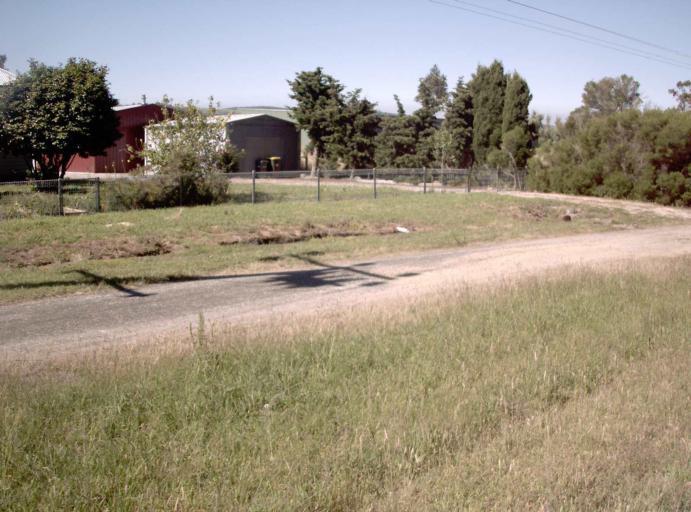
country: AU
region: Victoria
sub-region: Latrobe
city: Morwell
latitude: -38.6641
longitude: 146.4444
